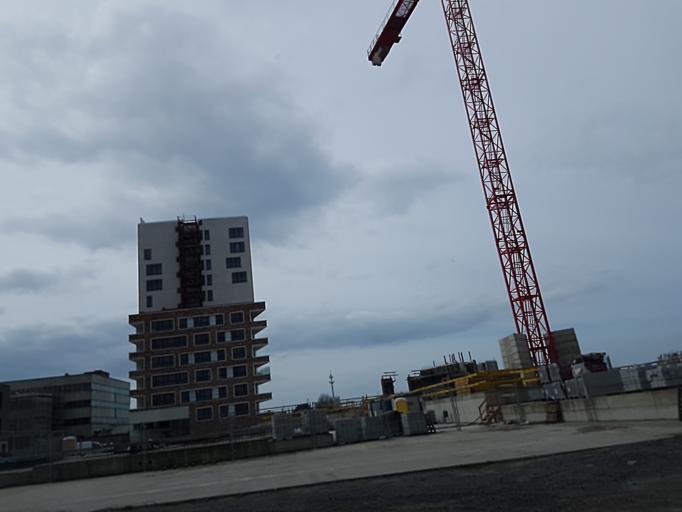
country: BE
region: Flanders
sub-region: Provincie West-Vlaanderen
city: Ostend
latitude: 51.2237
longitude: 2.9499
